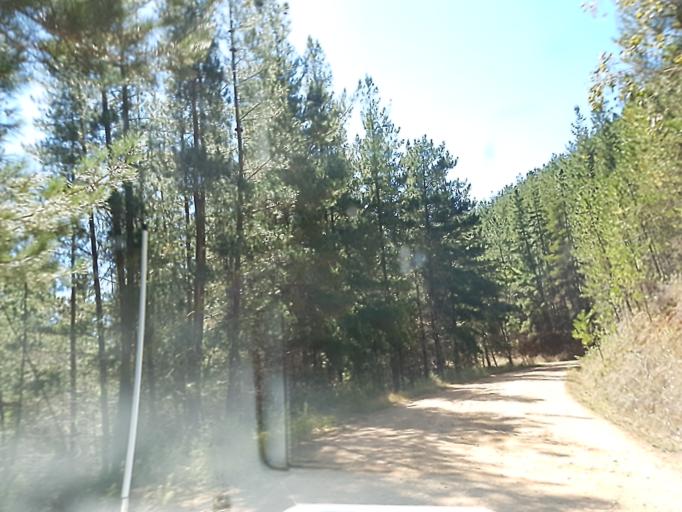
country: AU
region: Victoria
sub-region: Alpine
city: Mount Beauty
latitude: -36.7509
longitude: 146.9589
